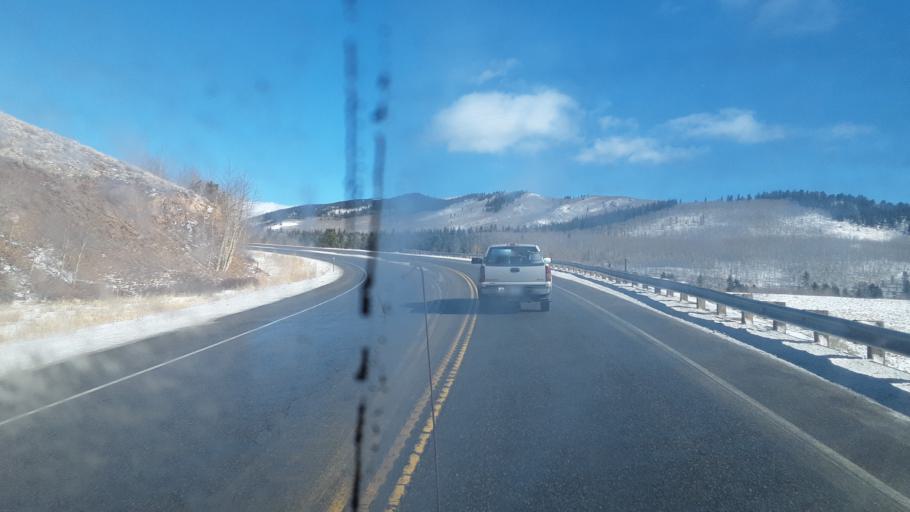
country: US
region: Colorado
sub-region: Summit County
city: Breckenridge
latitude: 39.4023
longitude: -105.7562
